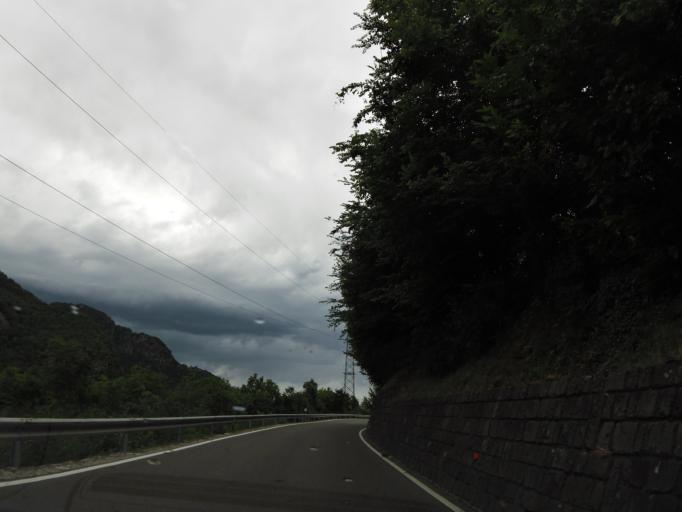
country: IT
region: Trentino-Alto Adige
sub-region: Bolzano
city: Collalbo
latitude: 46.5038
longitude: 11.4627
